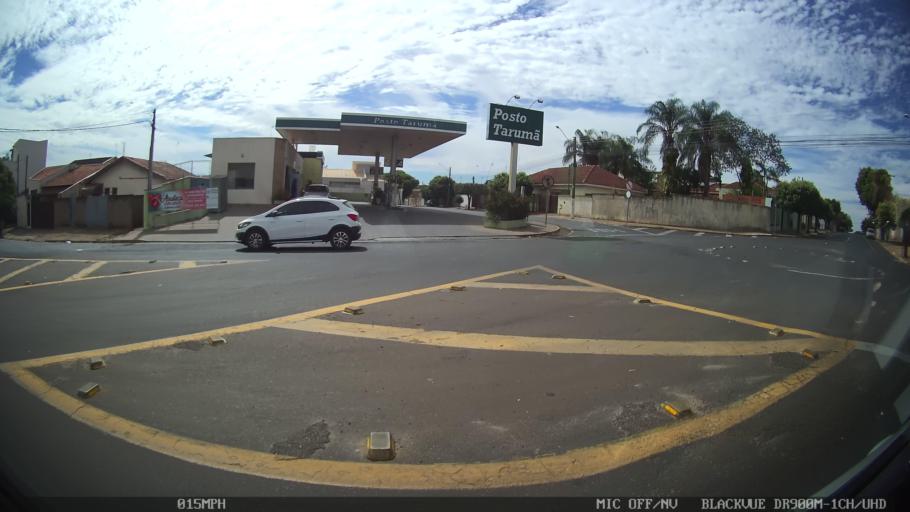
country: BR
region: Sao Paulo
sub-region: Catanduva
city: Catanduva
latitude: -21.1437
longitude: -48.9615
